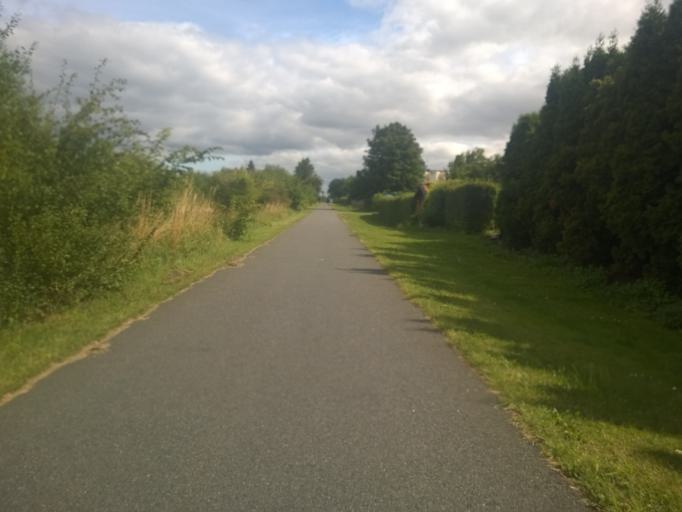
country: SE
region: Skane
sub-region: Kristianstads Kommun
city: Kristianstad
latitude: 56.0553
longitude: 14.1751
